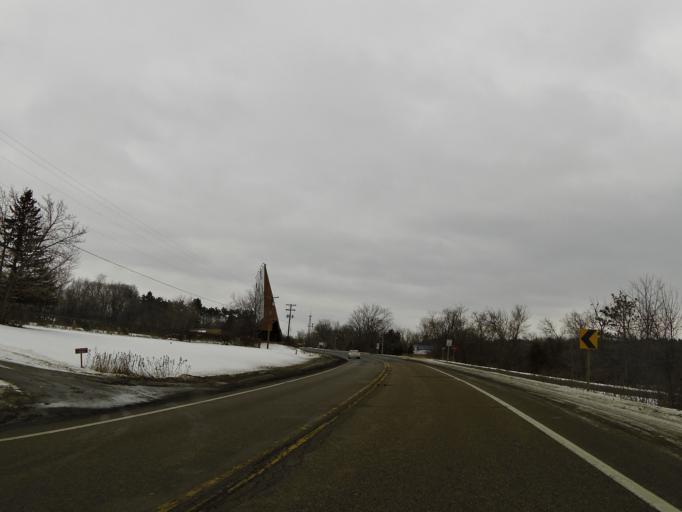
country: US
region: Minnesota
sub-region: Washington County
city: Stillwater
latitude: 45.0699
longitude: -92.7914
